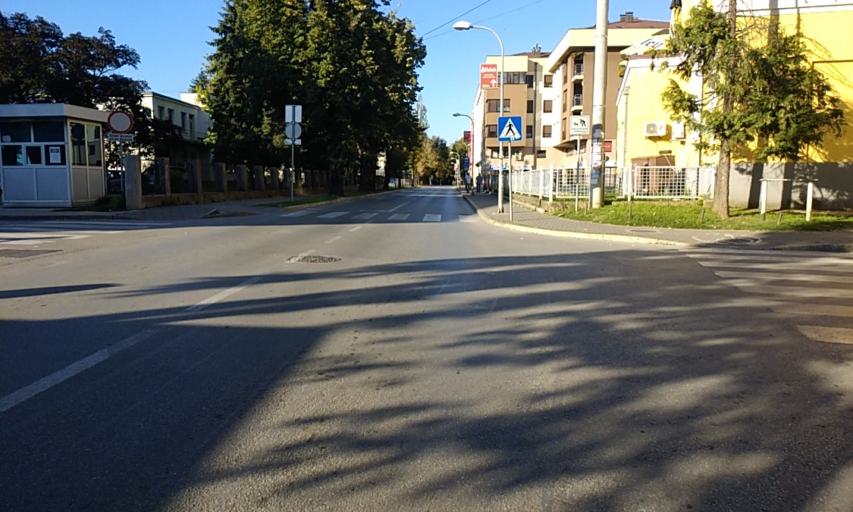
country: BA
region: Republika Srpska
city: Banja Luka
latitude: 44.7706
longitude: 17.1852
